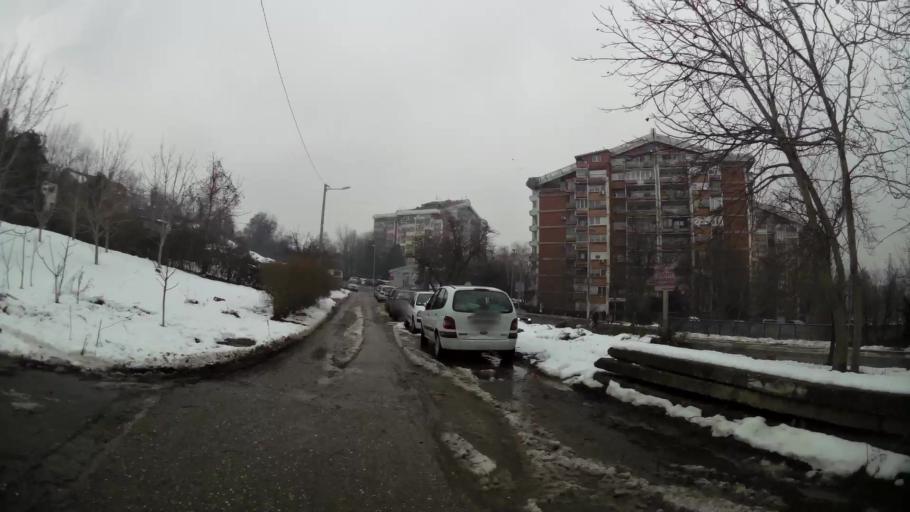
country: RS
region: Central Serbia
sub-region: Belgrade
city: Zvezdara
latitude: 44.7715
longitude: 20.5115
